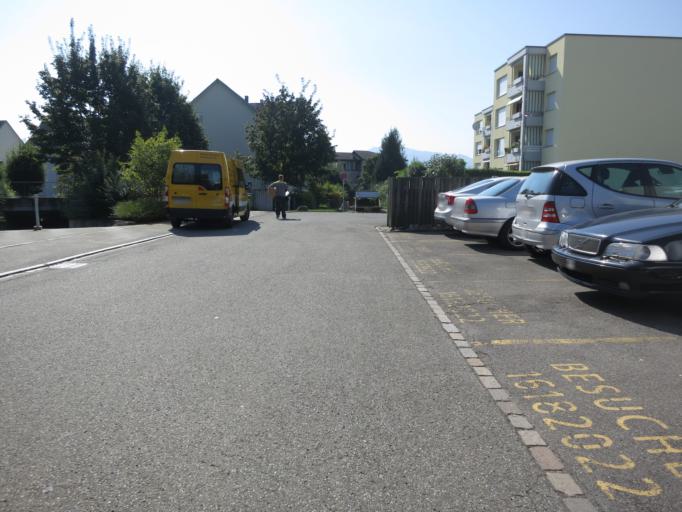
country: CH
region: Zurich
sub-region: Bezirk Meilen
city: Hombrechtikon
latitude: 47.2490
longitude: 8.7733
